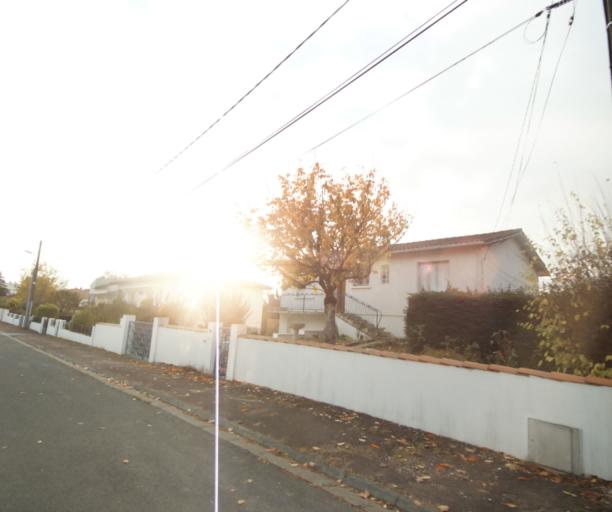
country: FR
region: Poitou-Charentes
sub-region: Departement de la Charente-Maritime
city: Saintes
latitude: 45.7524
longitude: -0.6461
